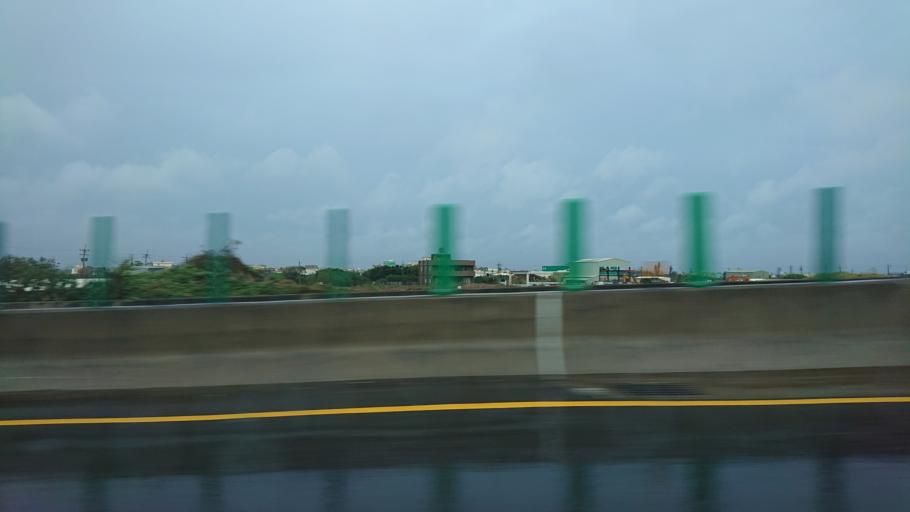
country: TW
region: Taiwan
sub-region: Changhua
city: Chang-hua
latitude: 24.1429
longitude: 120.4471
